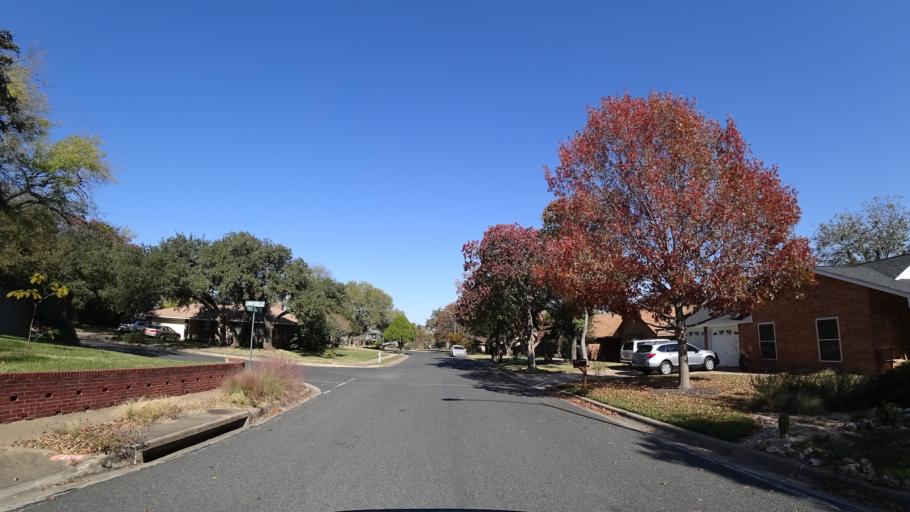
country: US
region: Texas
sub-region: Travis County
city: Shady Hollow
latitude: 30.2219
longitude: -97.8580
